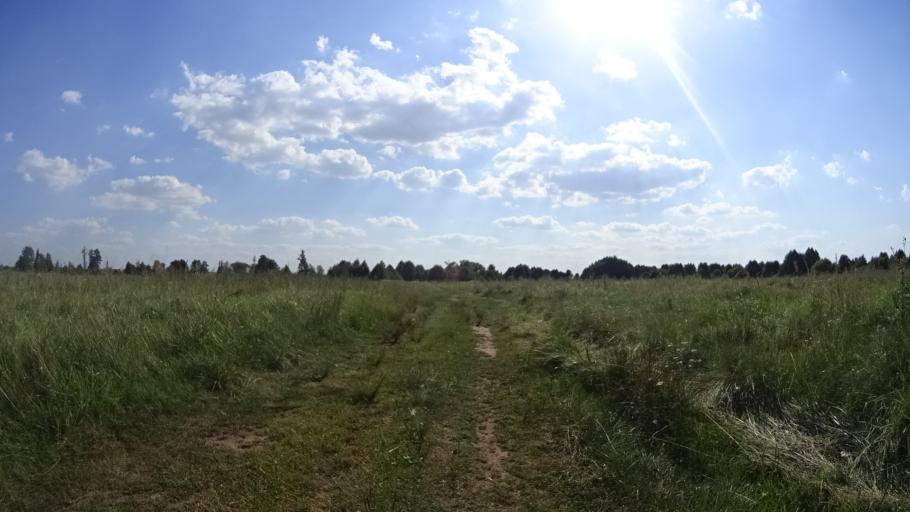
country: PL
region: Masovian Voivodeship
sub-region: Powiat bialobrzeski
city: Wysmierzyce
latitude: 51.6464
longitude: 20.8228
